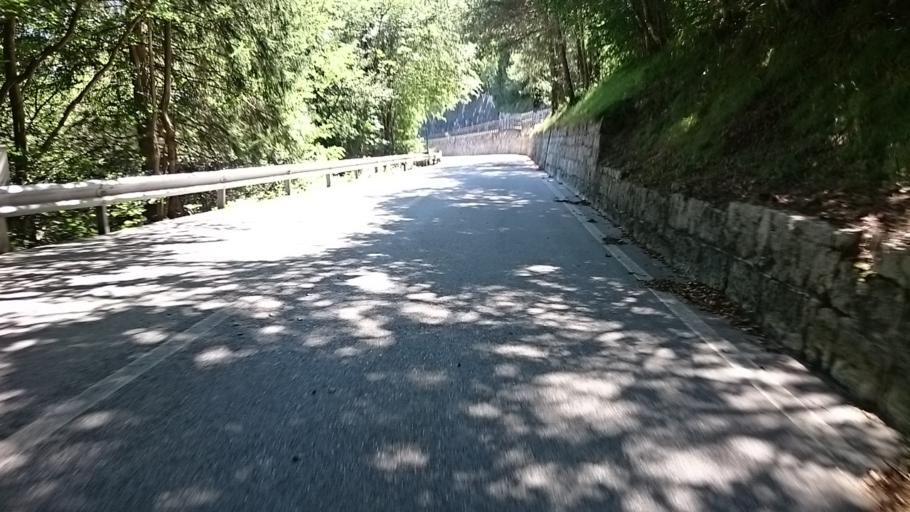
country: IT
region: Veneto
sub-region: Provincia di Belluno
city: Perarolo di Cadore
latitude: 46.3761
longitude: 12.3546
